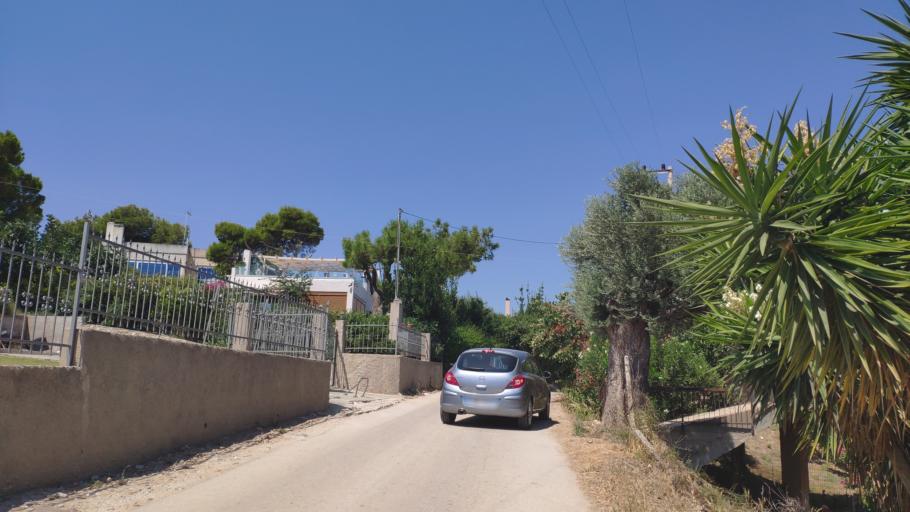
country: GR
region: Attica
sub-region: Nomarchia Anatolikis Attikis
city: Limin Mesoyaias
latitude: 37.8917
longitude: 24.0076
